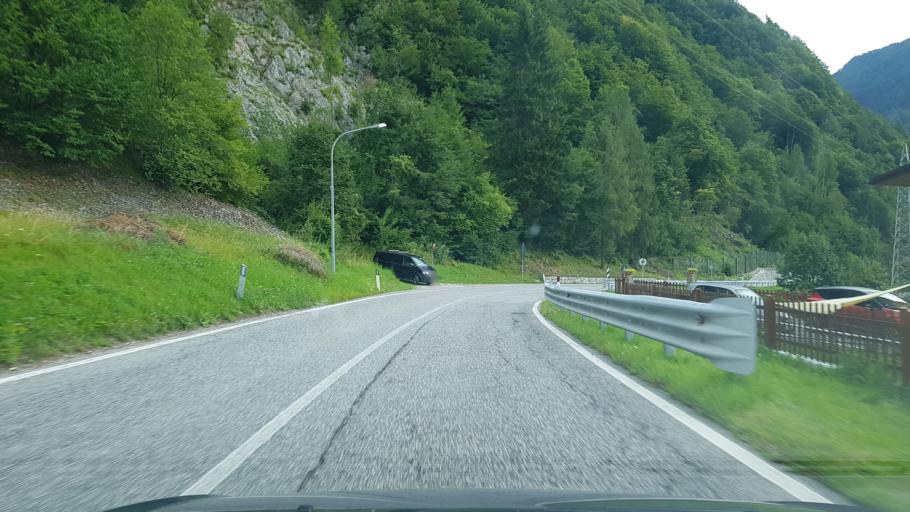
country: IT
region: Friuli Venezia Giulia
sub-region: Provincia di Udine
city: Forni Avoltri
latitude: 46.5844
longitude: 12.7650
